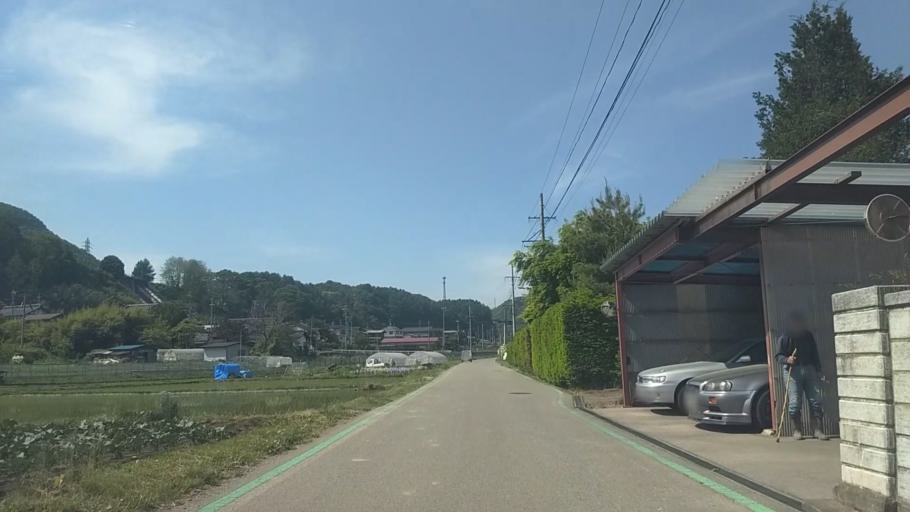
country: JP
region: Nagano
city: Saku
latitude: 36.1334
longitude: 138.4750
